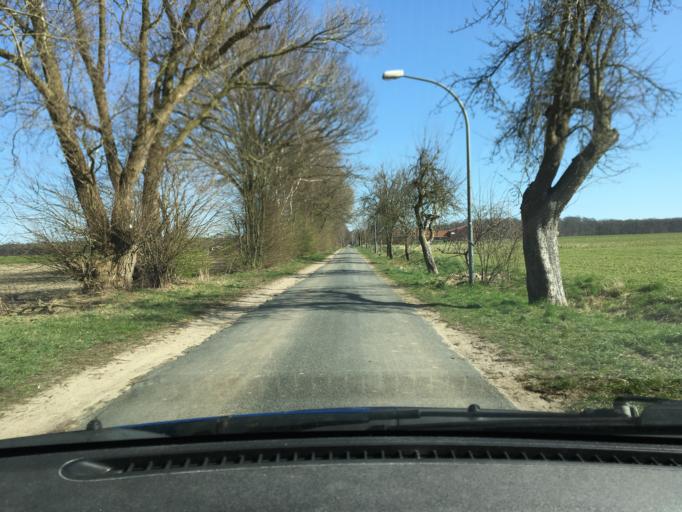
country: DE
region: Lower Saxony
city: Ebstorf
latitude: 53.0256
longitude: 10.4332
